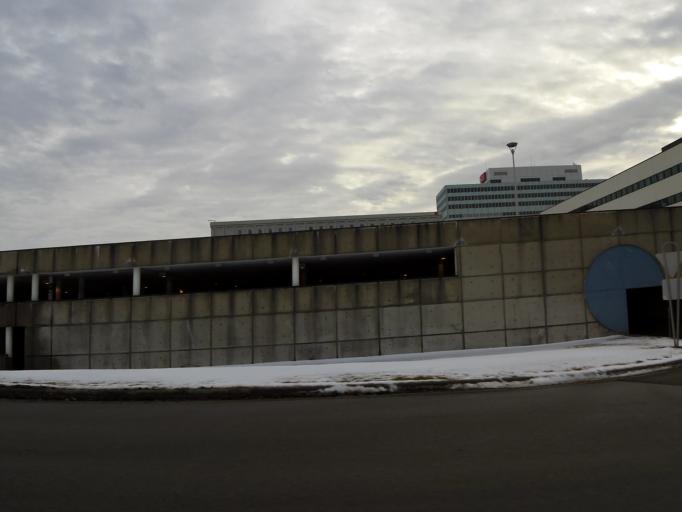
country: US
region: Minnesota
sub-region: Ramsey County
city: Maplewood
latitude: 44.9531
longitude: -92.9945
